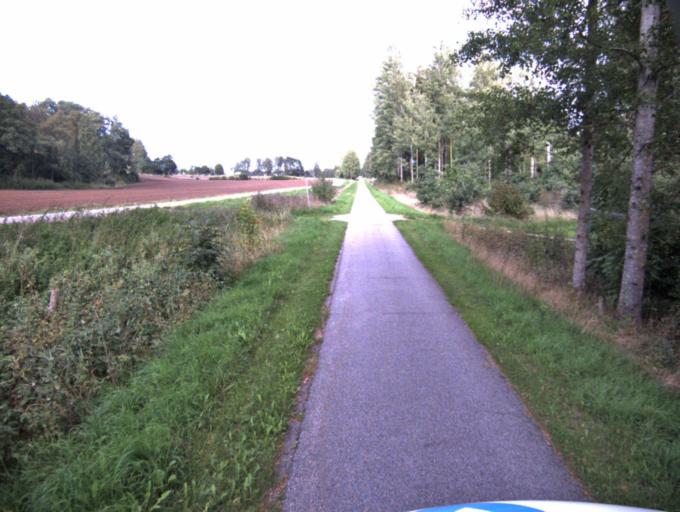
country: SE
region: Vaestra Goetaland
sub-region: Ulricehamns Kommun
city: Ulricehamn
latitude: 57.8457
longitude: 13.4227
